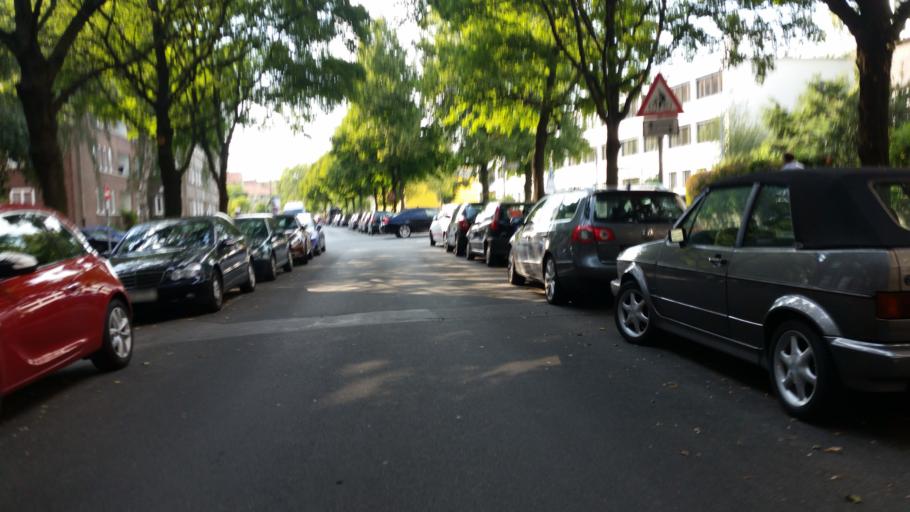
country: DE
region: Lower Saxony
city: Hannover
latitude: 52.3934
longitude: 9.7528
